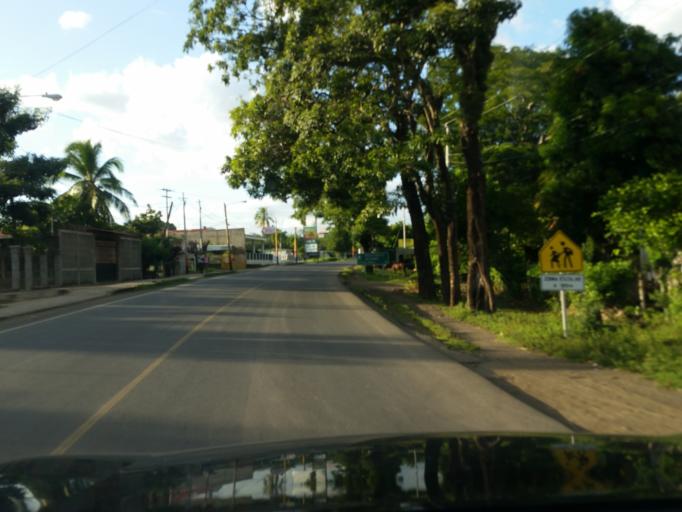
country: NI
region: Granada
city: Nandaime
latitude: 11.7555
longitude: -86.0449
